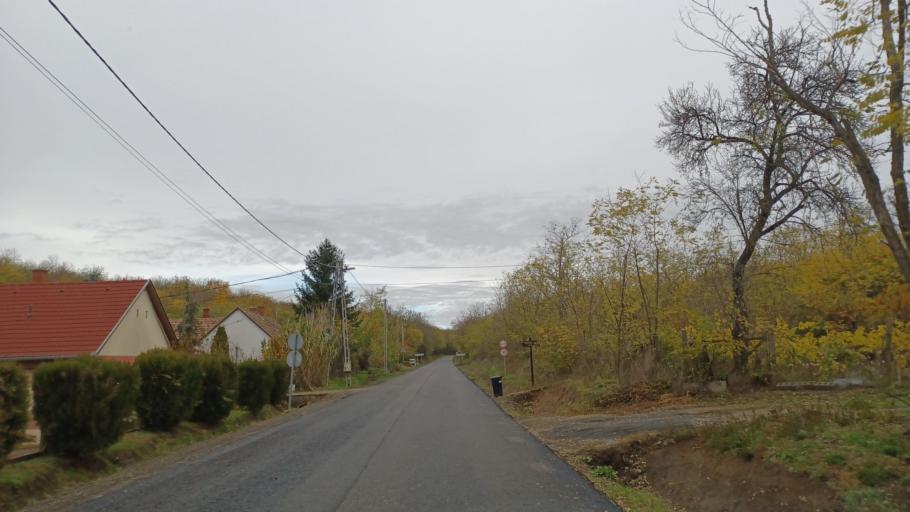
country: HU
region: Tolna
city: Dunaszentgyorgy
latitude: 46.5301
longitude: 18.7655
